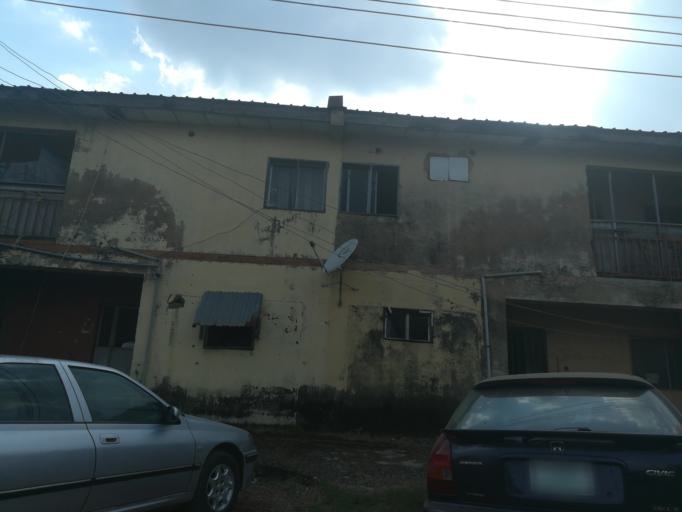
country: NG
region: Abuja Federal Capital Territory
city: Abuja
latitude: 9.0790
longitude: 7.4120
